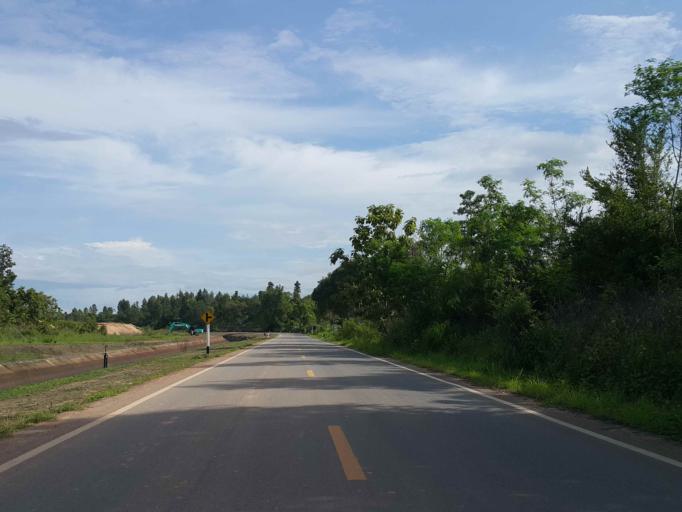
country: TH
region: Chiang Mai
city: San Sai
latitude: 18.9005
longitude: 99.1486
